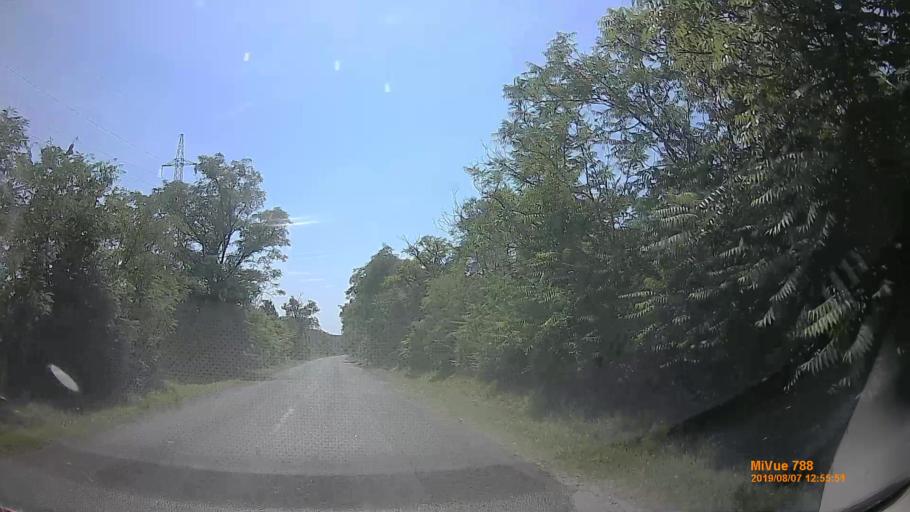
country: HU
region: Zala
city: Gyenesdias
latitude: 46.8049
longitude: 17.2704
